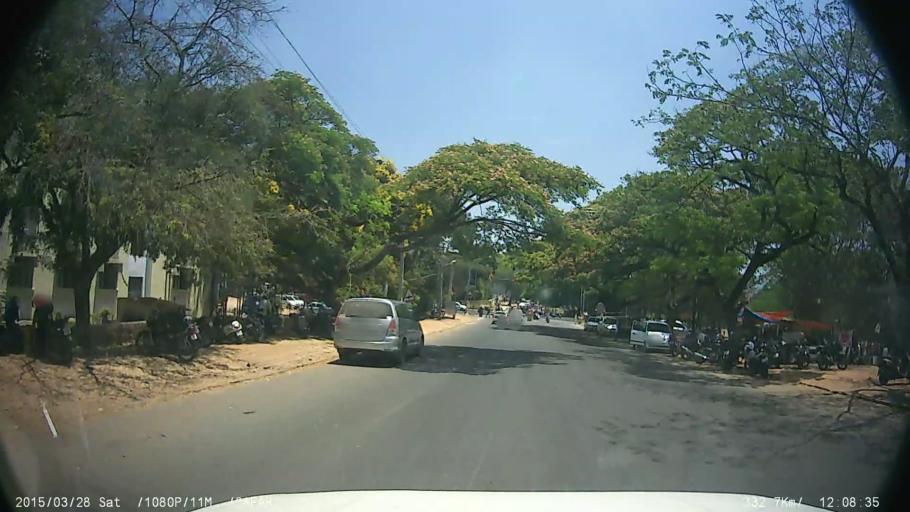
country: IN
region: Karnataka
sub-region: Mysore
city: Mysore
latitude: 12.3066
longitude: 76.6422
